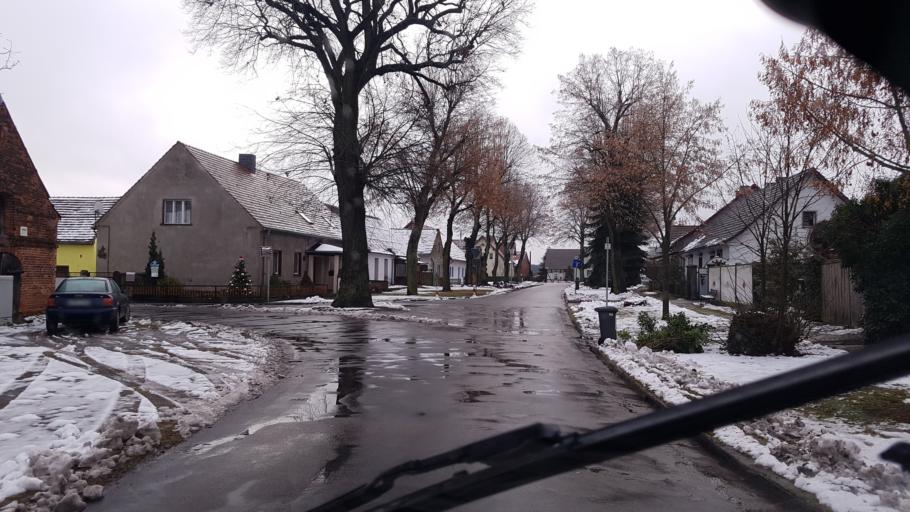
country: DE
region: Brandenburg
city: Neu Zauche
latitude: 51.9614
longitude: 14.1345
